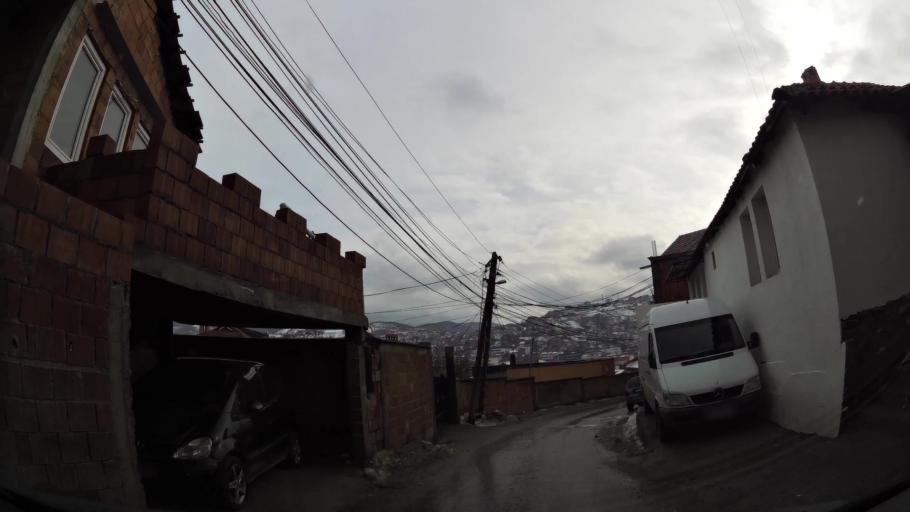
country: XK
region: Pristina
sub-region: Komuna e Prishtines
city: Pristina
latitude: 42.6804
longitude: 21.1712
